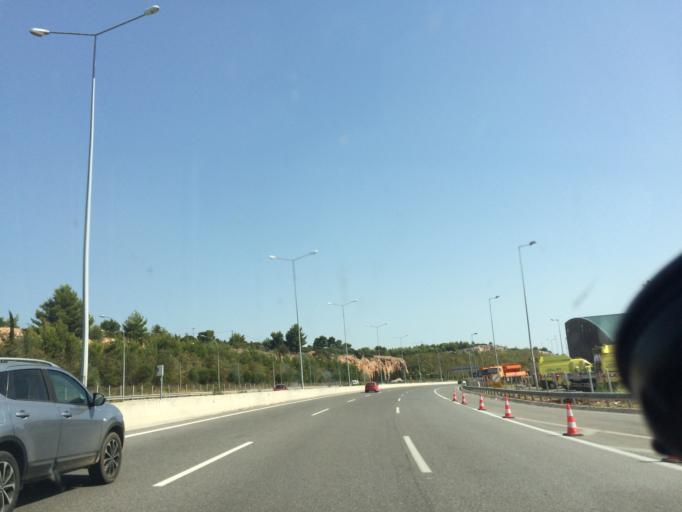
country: GR
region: Attica
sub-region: Nomarchia Anatolikis Attikis
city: Polydendri
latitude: 38.2279
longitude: 23.8466
